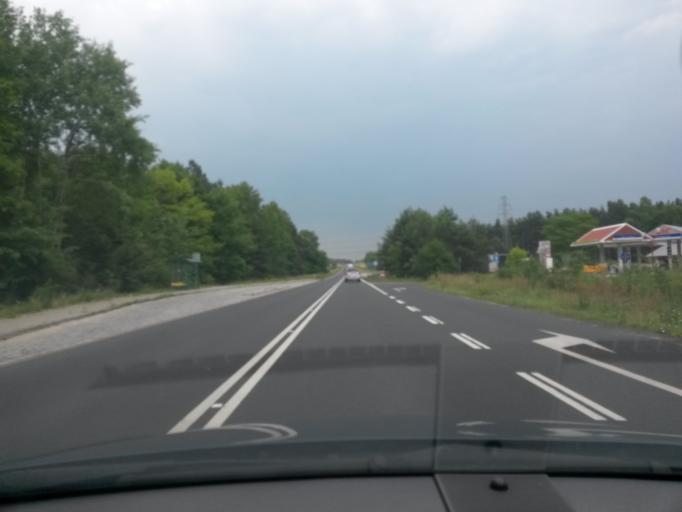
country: PL
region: Silesian Voivodeship
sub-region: Powiat czestochowski
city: Olsztyn
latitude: 50.7602
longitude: 19.2225
